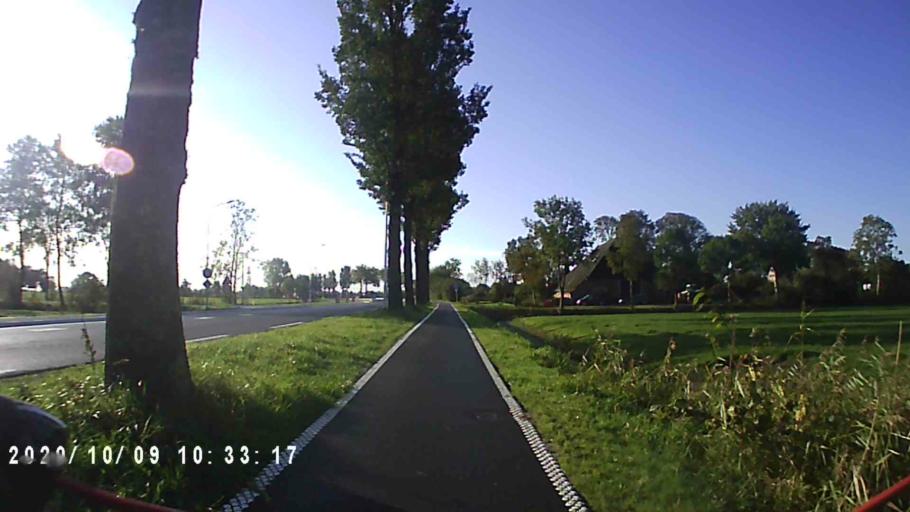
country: NL
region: Groningen
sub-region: Gemeente Winsum
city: Winsum
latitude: 53.3054
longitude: 6.5318
